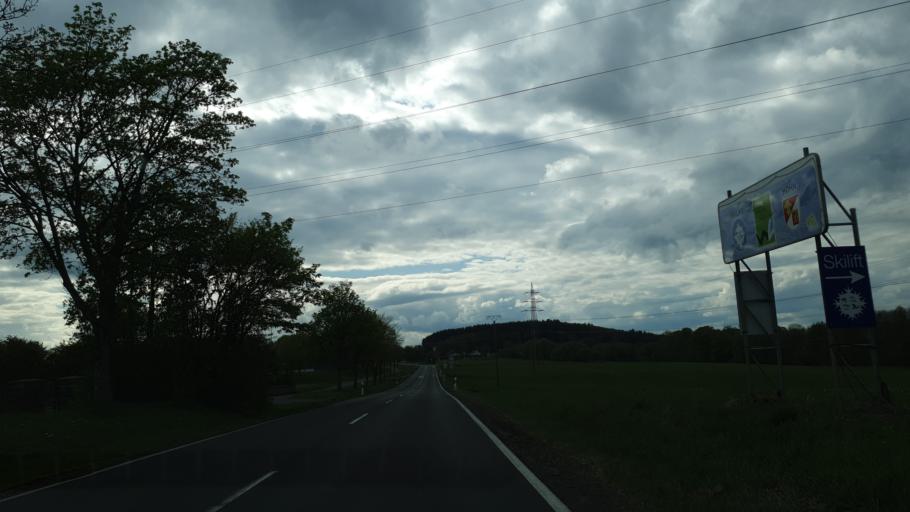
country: DE
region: Rheinland-Pfalz
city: Grossseifen
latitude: 50.6223
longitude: 7.9671
